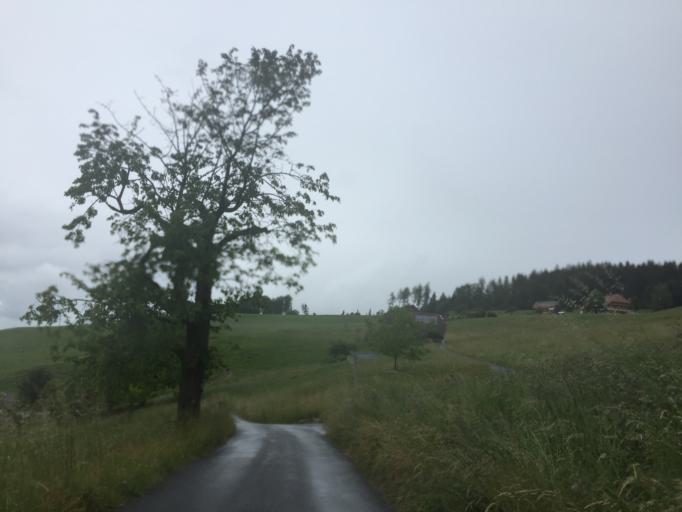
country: CH
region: Bern
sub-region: Bern-Mittelland District
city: Taegertschi
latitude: 46.8901
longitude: 7.6003
